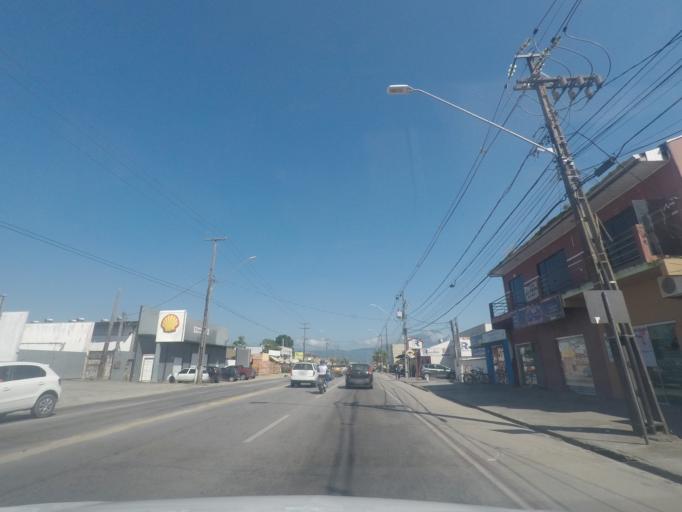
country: BR
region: Parana
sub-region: Paranagua
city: Paranagua
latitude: -25.5595
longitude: -48.5602
